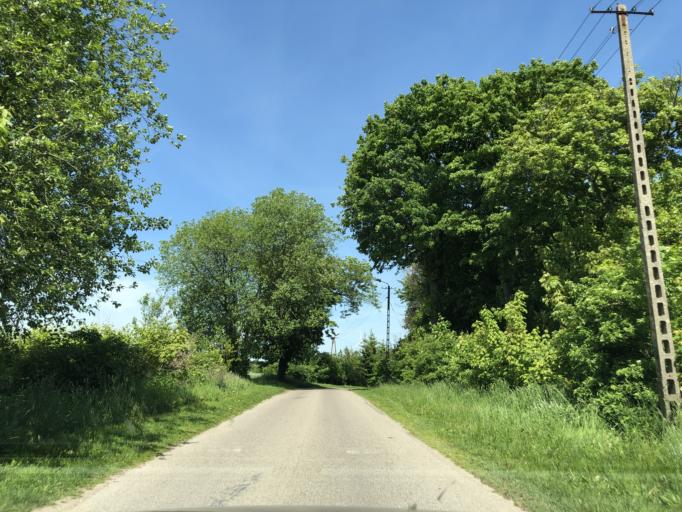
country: PL
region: West Pomeranian Voivodeship
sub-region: Powiat kolobrzeski
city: Goscino
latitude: 54.0467
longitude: 15.7271
